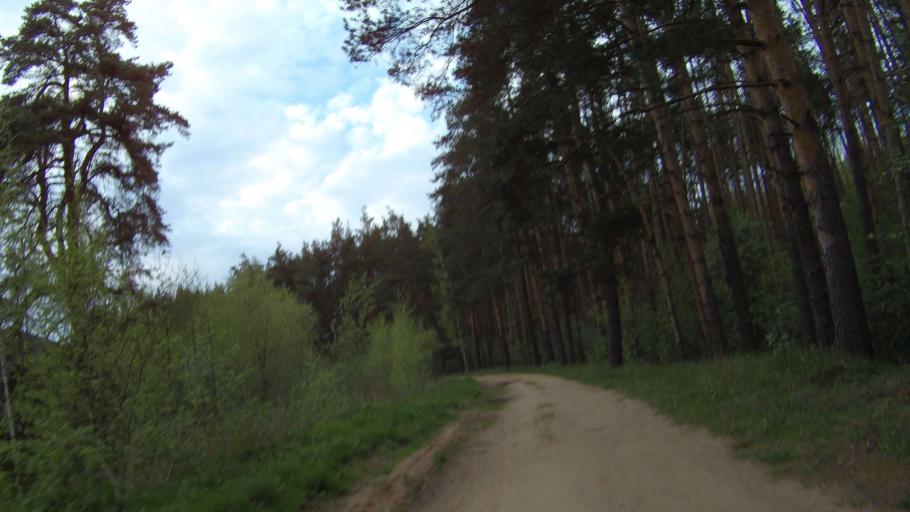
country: RU
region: Moskovskaya
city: Ramenskoye
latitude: 55.5859
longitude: 38.2228
